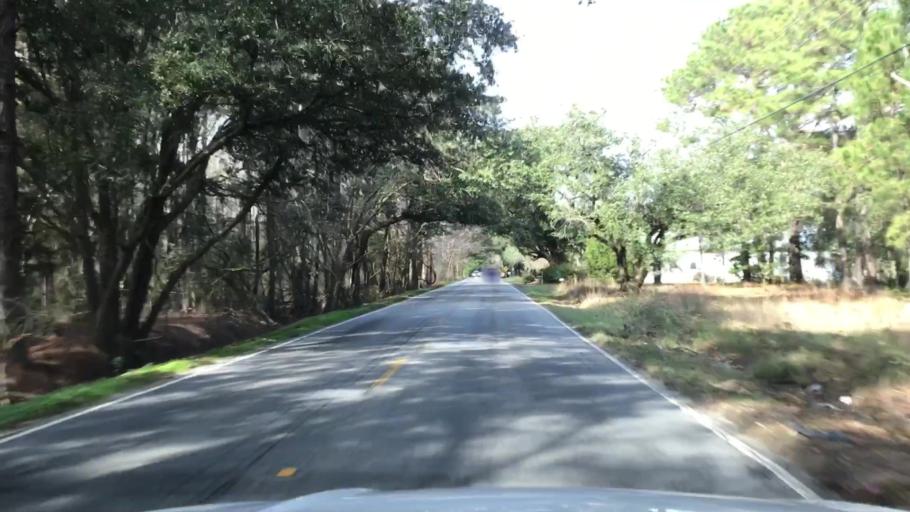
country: US
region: South Carolina
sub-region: Charleston County
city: Shell Point
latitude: 32.7614
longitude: -80.0582
